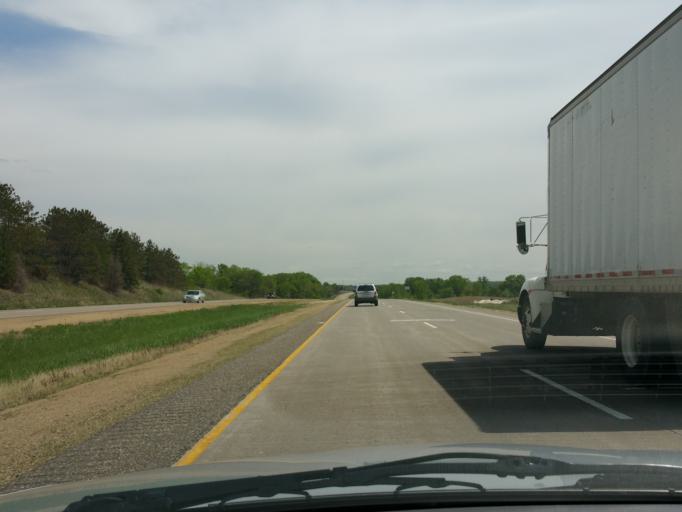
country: US
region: Wisconsin
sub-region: Pierce County
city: River Falls
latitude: 44.9253
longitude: -92.6782
